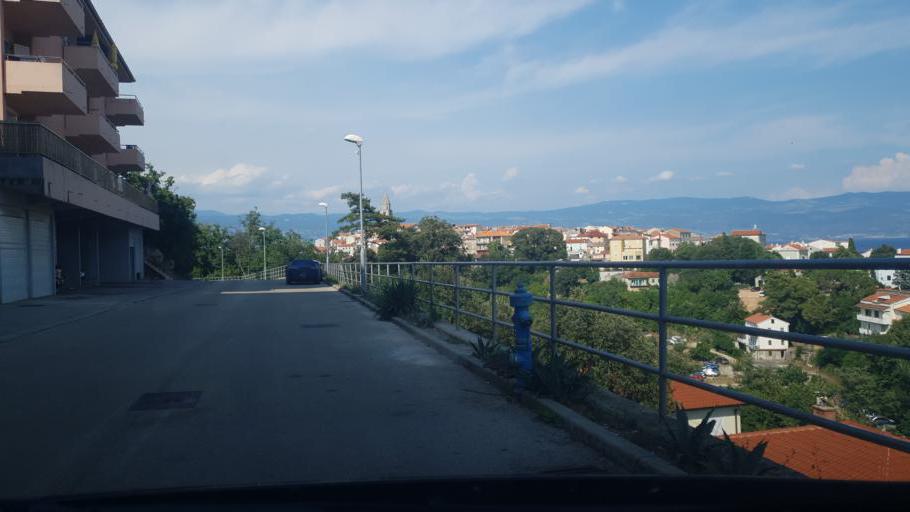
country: HR
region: Primorsko-Goranska
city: Punat
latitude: 45.0749
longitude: 14.6708
